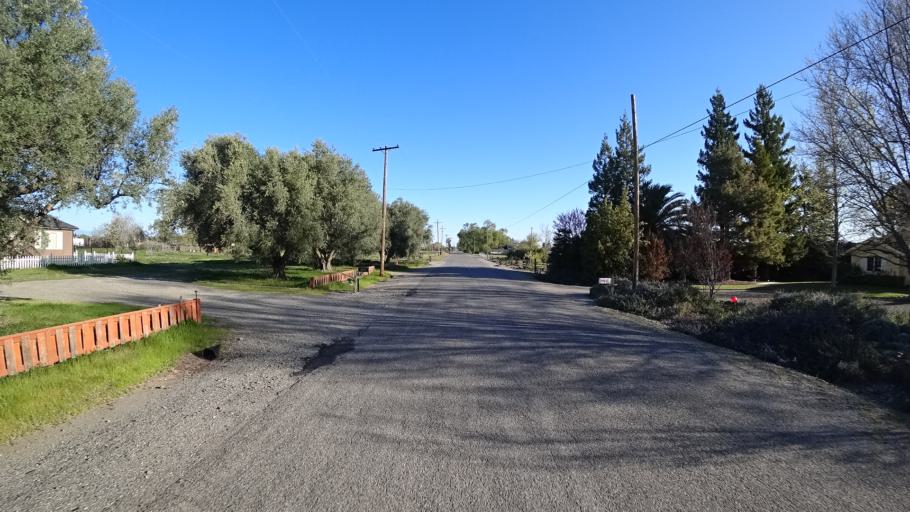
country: US
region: California
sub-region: Glenn County
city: Orland
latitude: 39.7617
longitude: -122.2297
